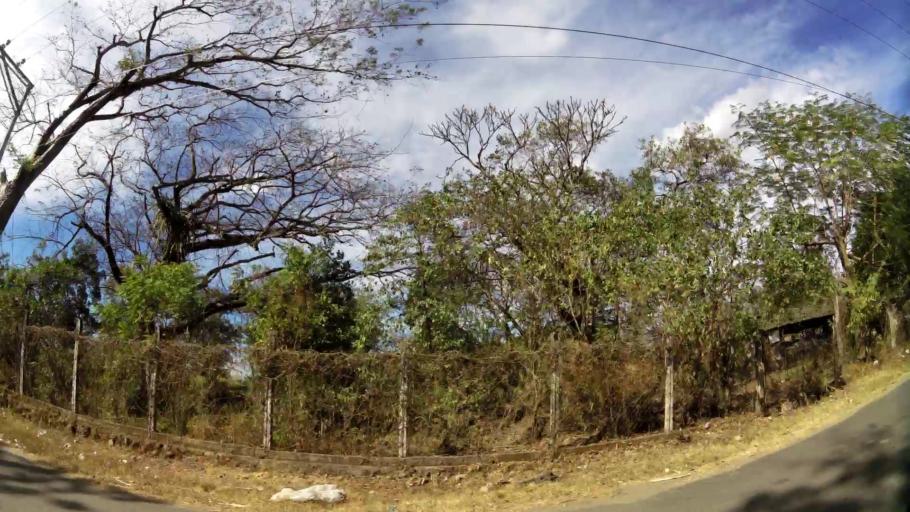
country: SV
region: San Salvador
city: Aguilares
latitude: 13.9647
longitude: -89.1157
